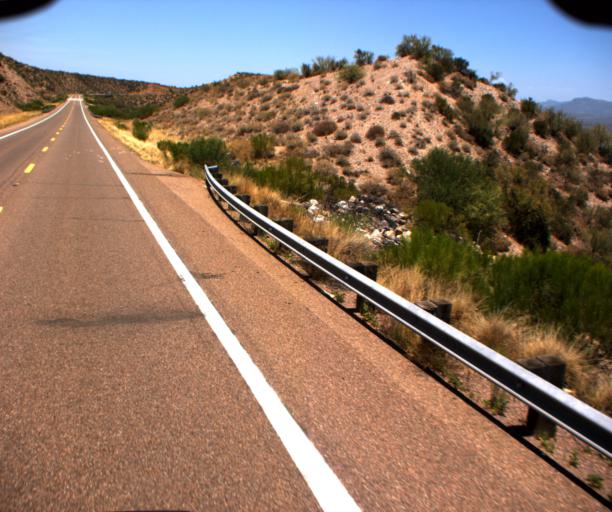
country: US
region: Arizona
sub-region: Gila County
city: Tonto Basin
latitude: 33.7104
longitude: -111.1994
